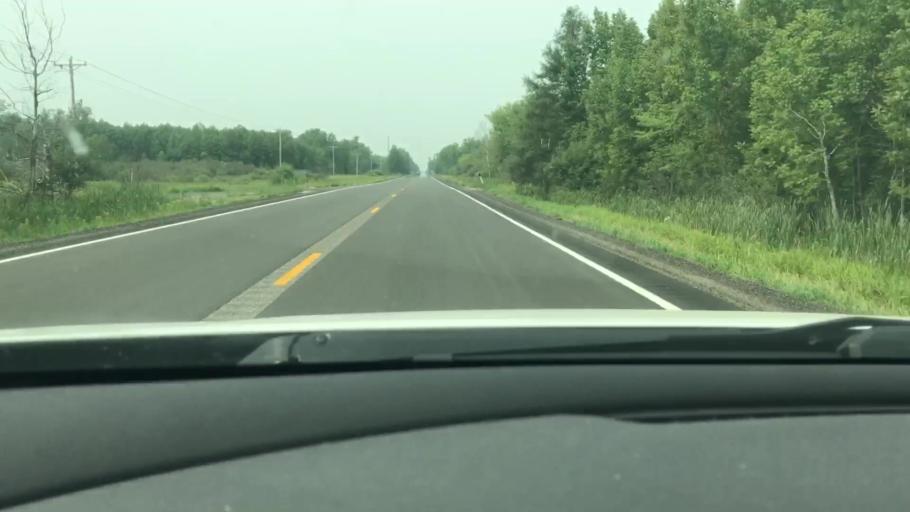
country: US
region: Minnesota
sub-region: Itasca County
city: Cohasset
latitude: 47.3636
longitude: -93.8701
